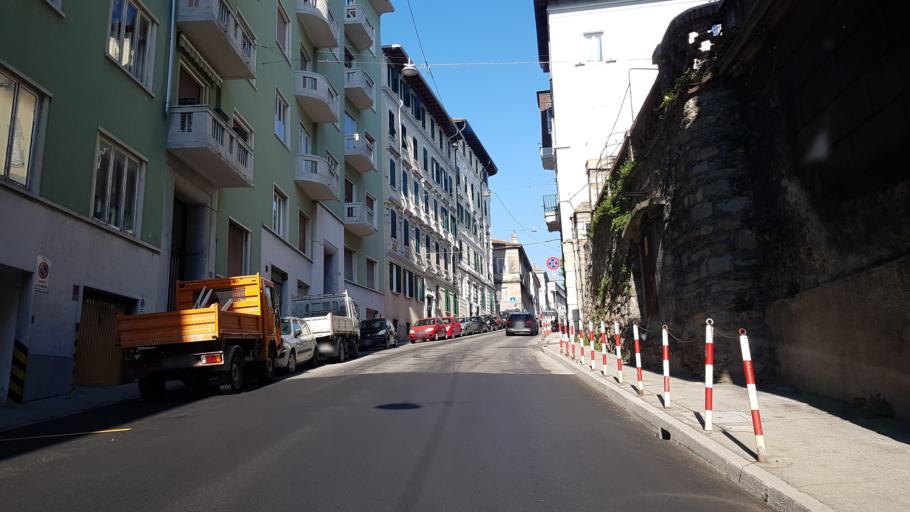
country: IT
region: Friuli Venezia Giulia
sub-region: Provincia di Trieste
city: Trieste
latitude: 45.6589
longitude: 13.7752
